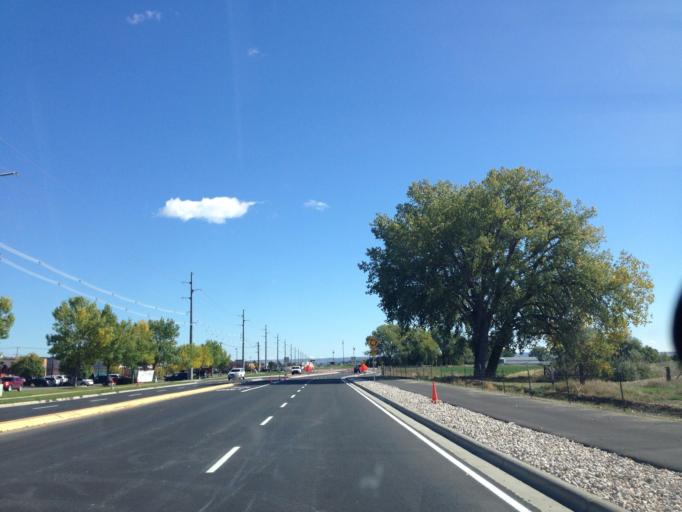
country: US
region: Montana
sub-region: Yellowstone County
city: Billings
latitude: 45.7840
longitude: -108.6144
